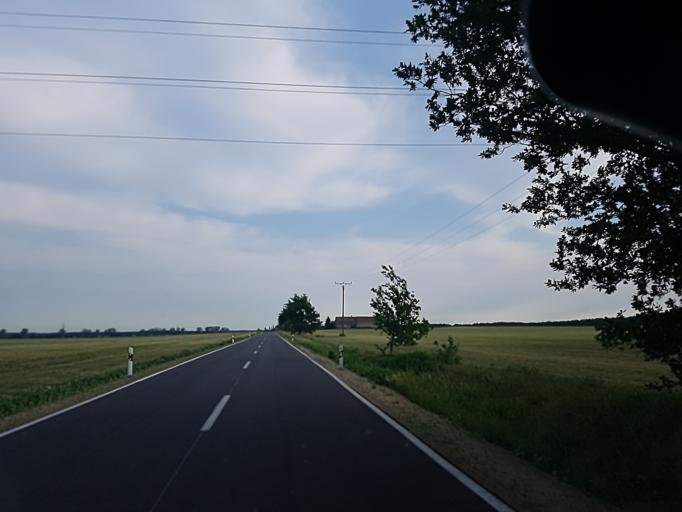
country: DE
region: Saxony-Anhalt
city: Jessen
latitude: 51.8063
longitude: 12.9529
